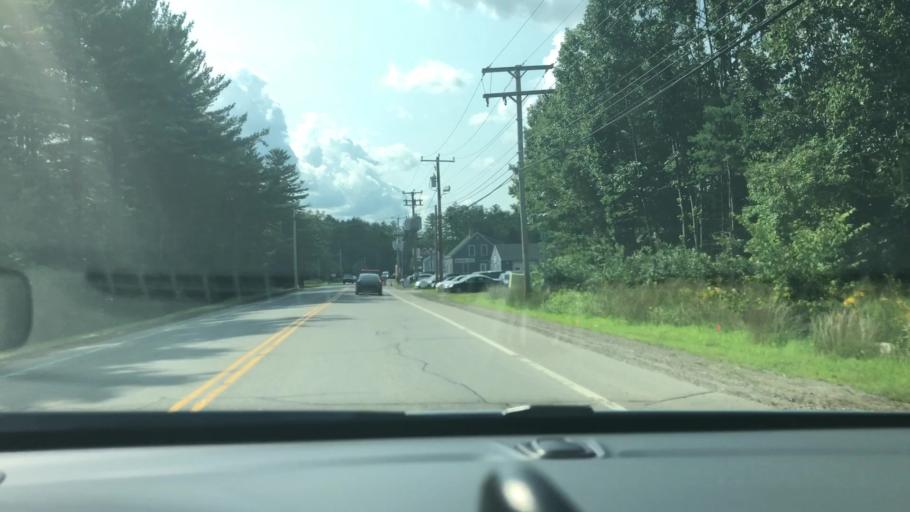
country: US
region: New Hampshire
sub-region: Hillsborough County
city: Pinardville
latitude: 43.0124
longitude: -71.5496
